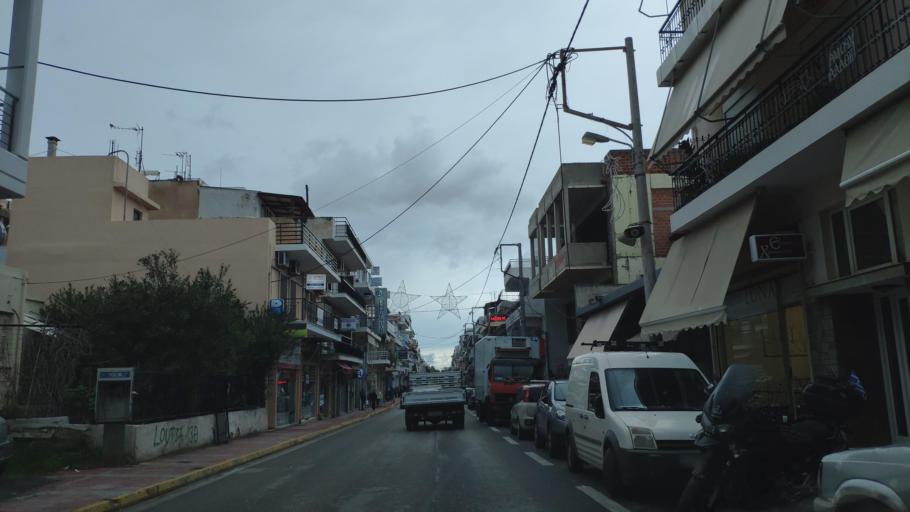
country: GR
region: Attica
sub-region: Nomarchia Anatolikis Attikis
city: Artemida
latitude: 37.9747
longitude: 24.0084
